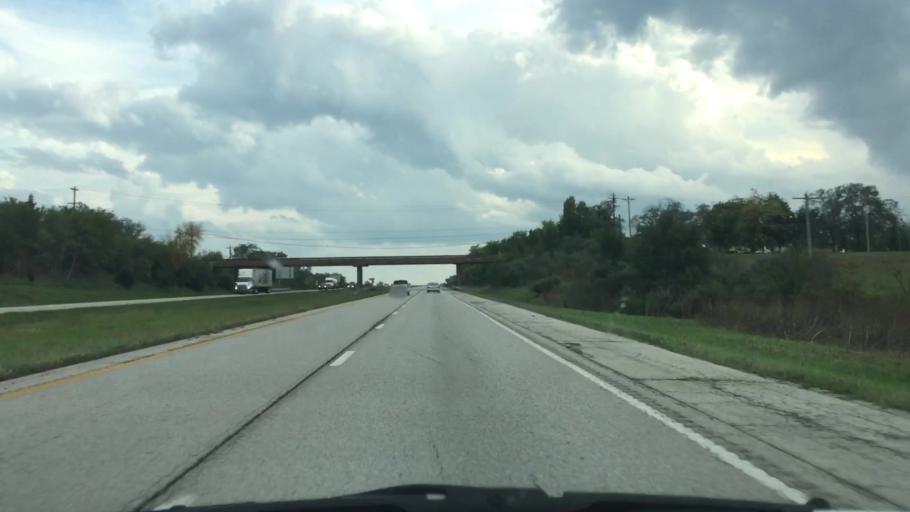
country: US
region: Missouri
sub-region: Clinton County
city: Cameron
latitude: 39.7440
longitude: -94.2203
